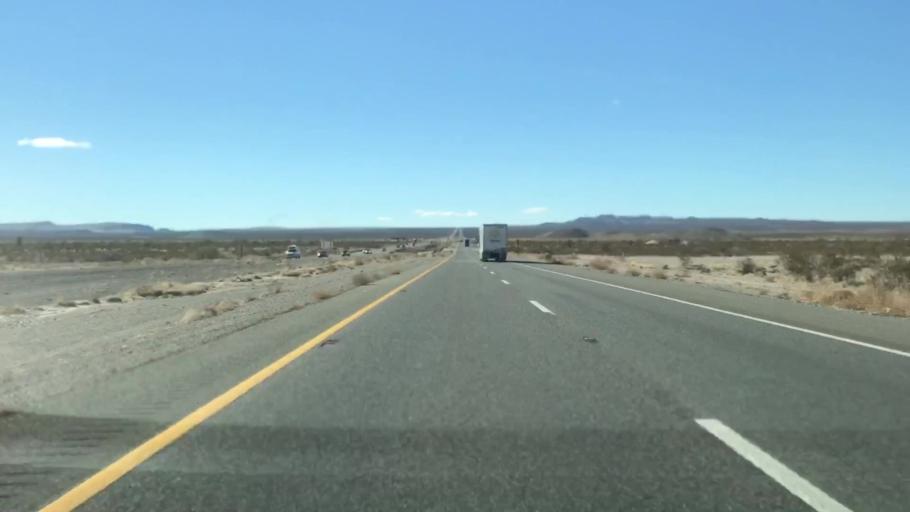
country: US
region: Nevada
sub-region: Clark County
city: Sandy Valley
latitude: 35.4438
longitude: -115.6754
